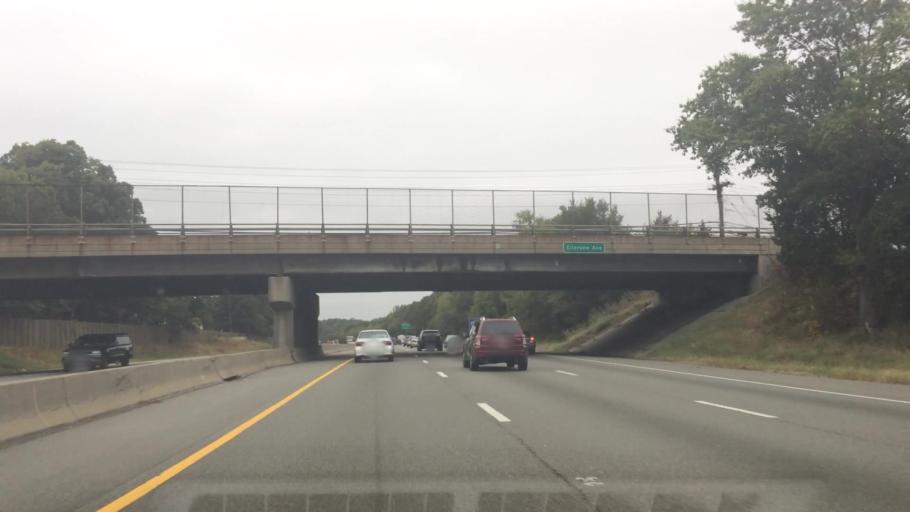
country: US
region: Virginia
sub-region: City of Colonial Heights
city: Colonial Heights
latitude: 37.2656
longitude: -77.3968
